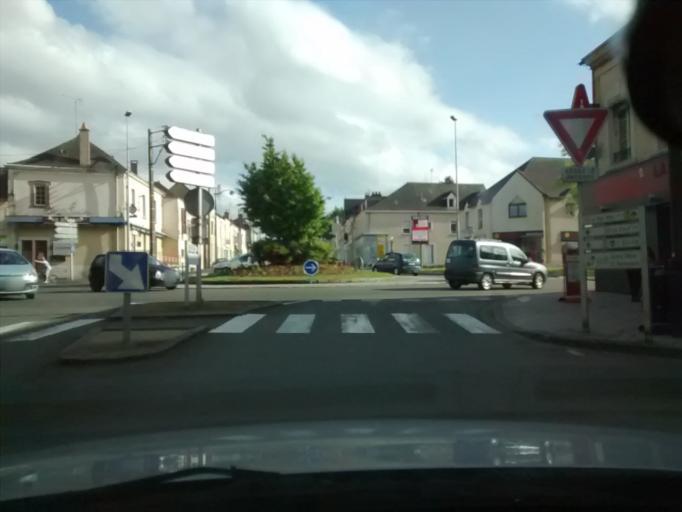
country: FR
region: Pays de la Loire
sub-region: Departement de la Mayenne
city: Chateau-Gontier
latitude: 47.8236
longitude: -0.7080
